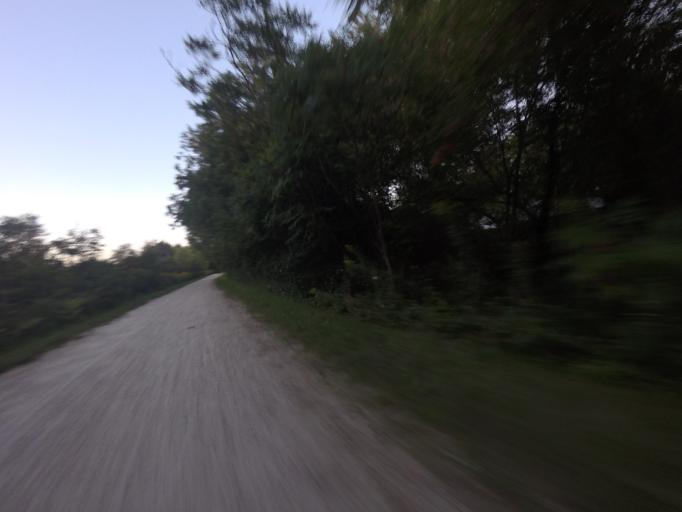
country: CA
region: Ontario
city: Orangeville
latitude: 43.9557
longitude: -79.8330
